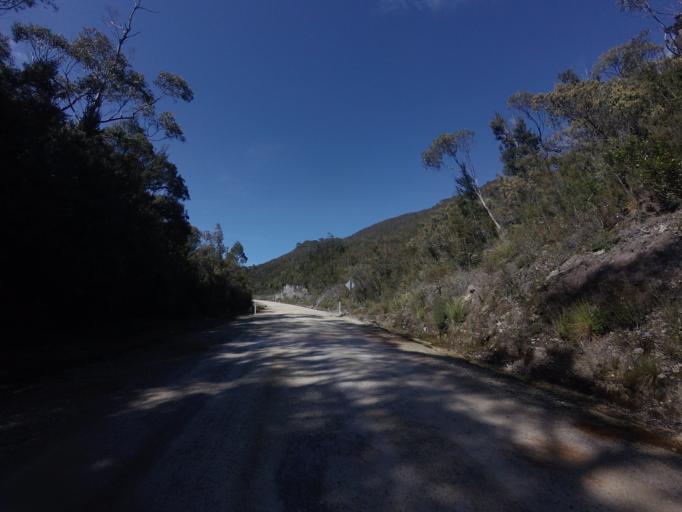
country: AU
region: Tasmania
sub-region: Huon Valley
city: Geeveston
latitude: -42.8156
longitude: 146.3860
